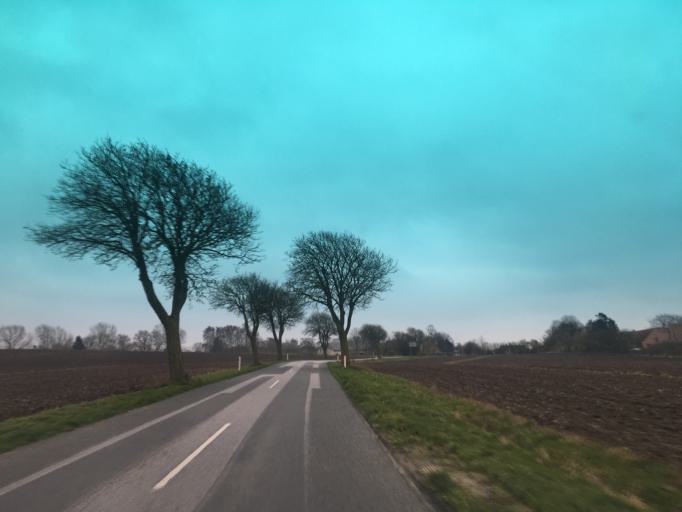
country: DK
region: Zealand
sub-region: Slagelse Kommune
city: Skaelskor
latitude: 55.2421
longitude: 11.4239
